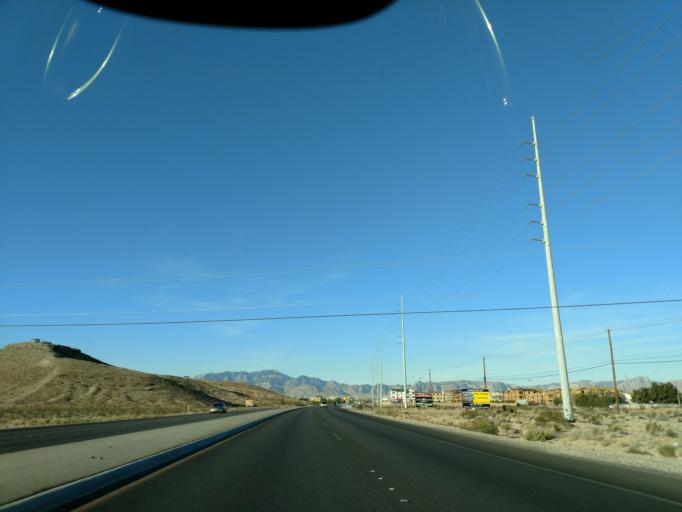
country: US
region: Nevada
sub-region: Clark County
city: Enterprise
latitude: 36.0209
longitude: -115.2524
